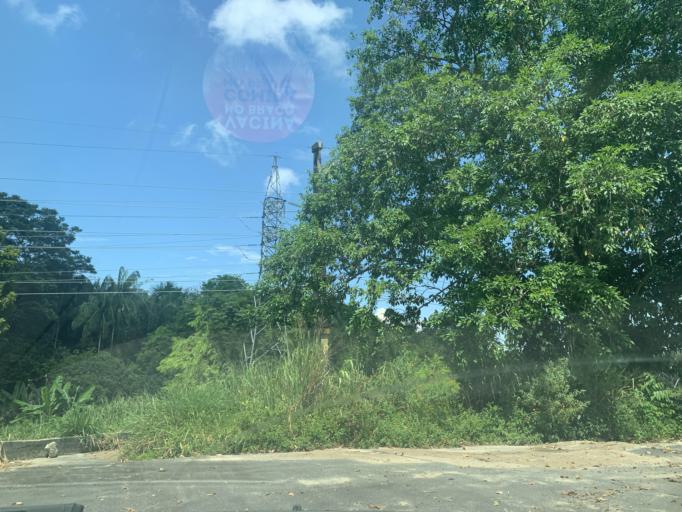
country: BR
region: Amazonas
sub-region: Manaus
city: Manaus
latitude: -3.1122
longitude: -59.9705
